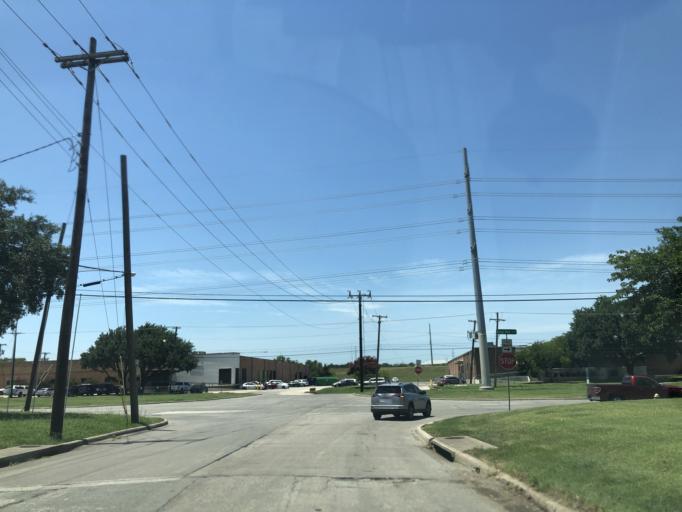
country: US
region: Texas
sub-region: Dallas County
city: Irving
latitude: 32.8193
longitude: -96.8951
